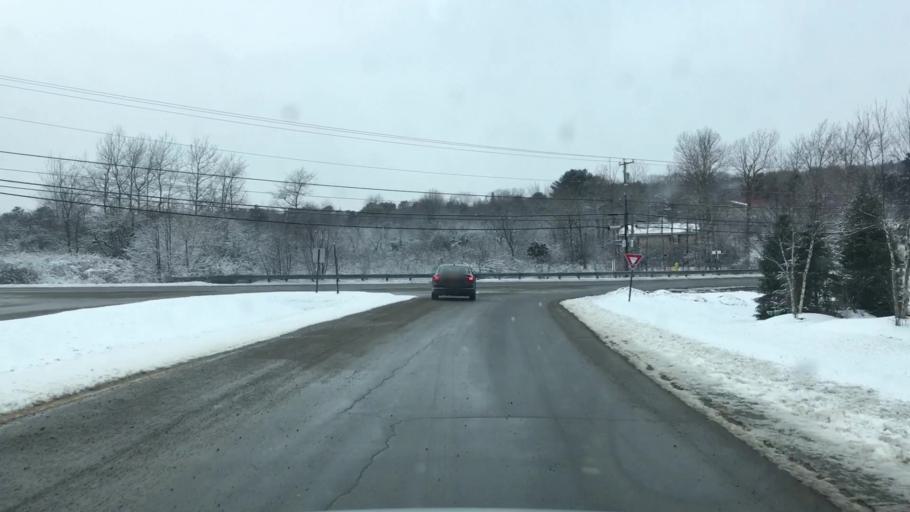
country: US
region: Maine
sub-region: Knox County
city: Rockland
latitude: 44.0765
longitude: -69.1046
